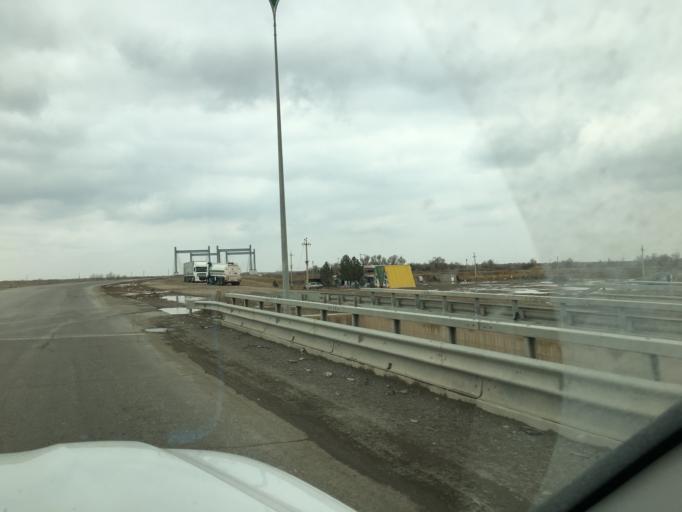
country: TM
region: Ahal
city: Tejen
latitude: 37.2321
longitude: 60.8621
